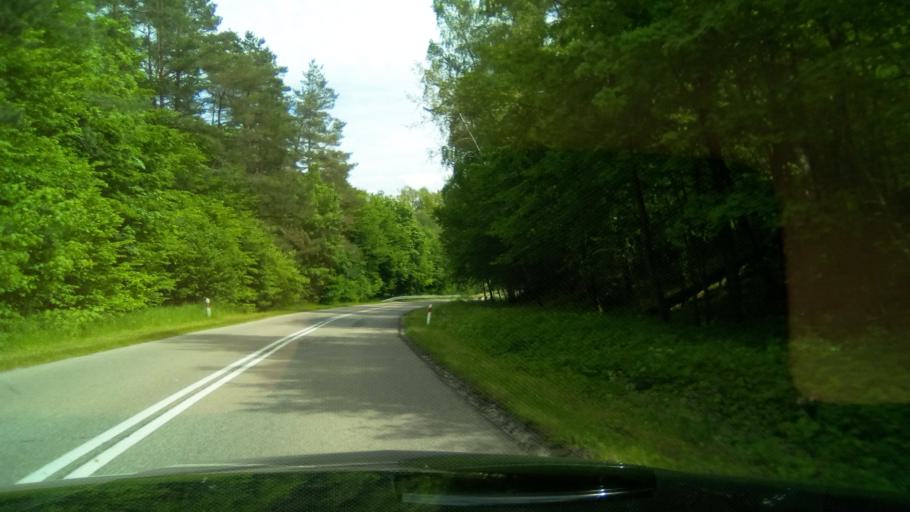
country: PL
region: Pomeranian Voivodeship
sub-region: Powiat leborski
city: Cewice
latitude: 54.3919
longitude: 17.6898
